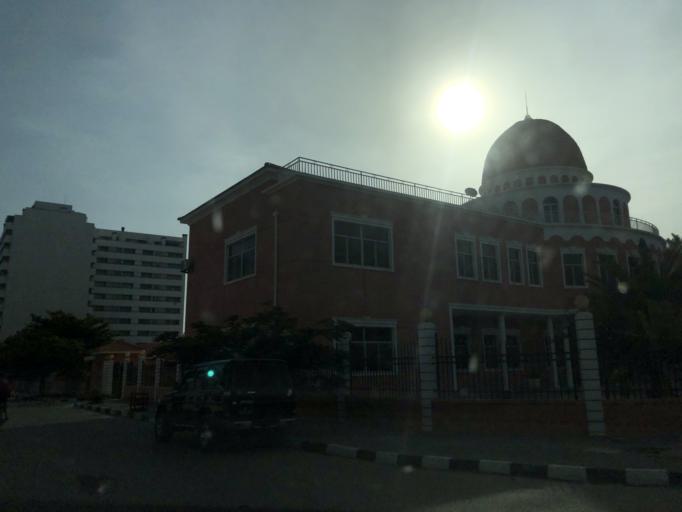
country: AO
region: Benguela
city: Benguela
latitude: -12.5782
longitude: 13.3967
